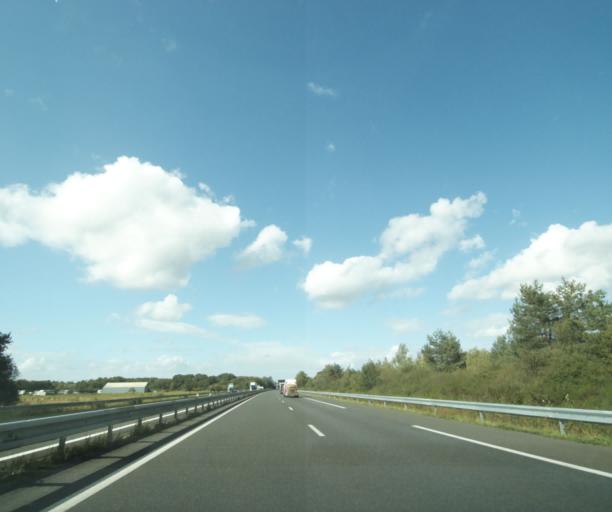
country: FR
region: Centre
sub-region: Departement du Loiret
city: Jouy-le-Potier
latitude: 47.7622
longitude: 1.8535
